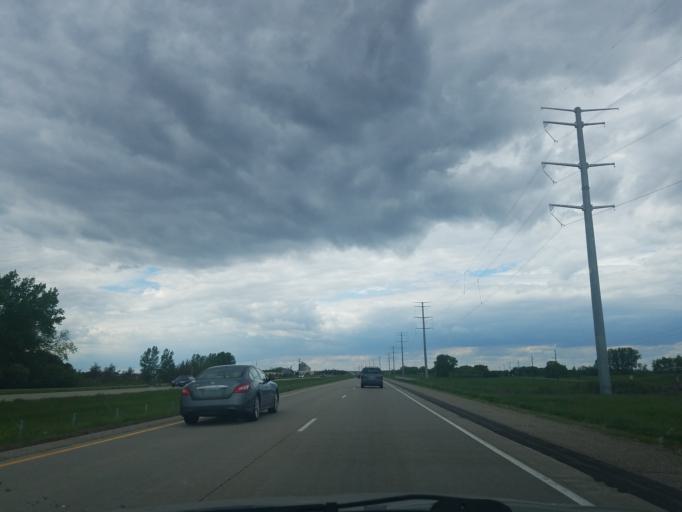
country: US
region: Minnesota
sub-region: Stearns County
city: Sauk Centre
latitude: 45.7695
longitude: -95.0407
